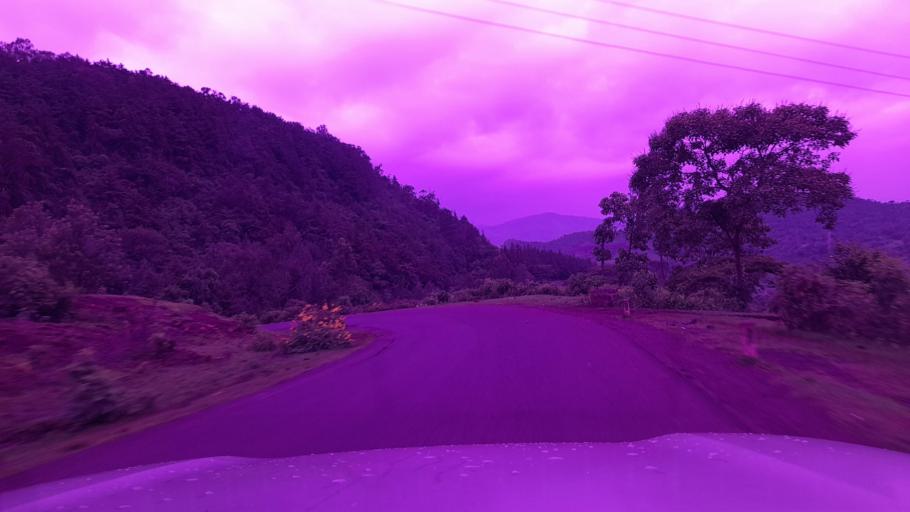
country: ET
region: Oromiya
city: Jima
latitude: 7.9312
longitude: 37.4313
